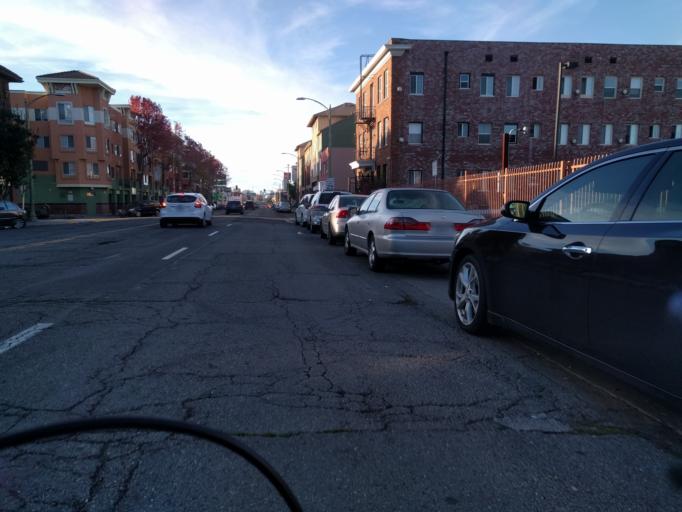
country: US
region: California
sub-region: Alameda County
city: Alameda
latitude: 37.7812
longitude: -122.2321
